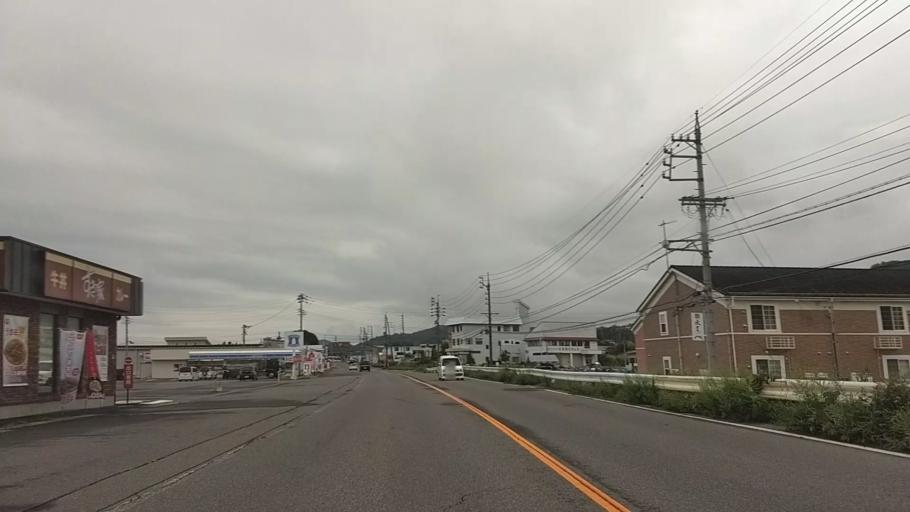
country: JP
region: Nagano
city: Iiyama
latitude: 36.8305
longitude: 138.3549
